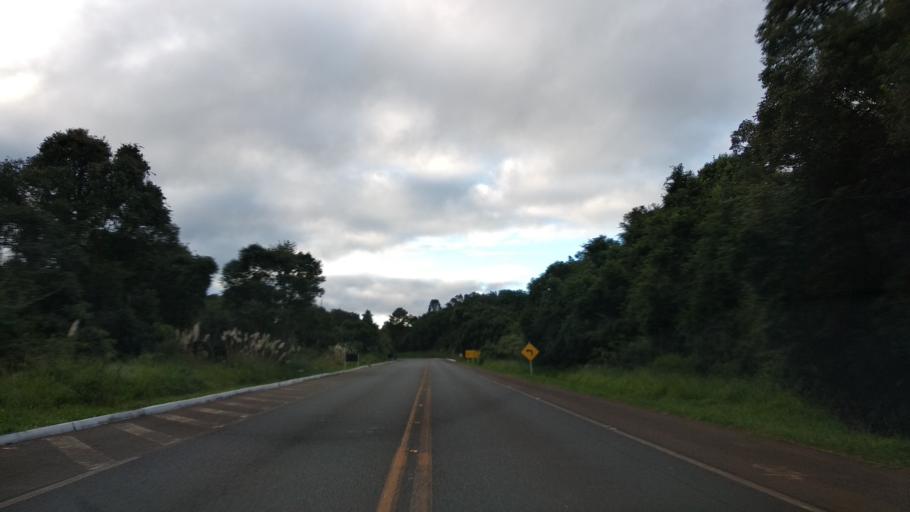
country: BR
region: Santa Catarina
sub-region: Campos Novos
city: Campos Novos
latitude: -27.5327
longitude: -50.8746
